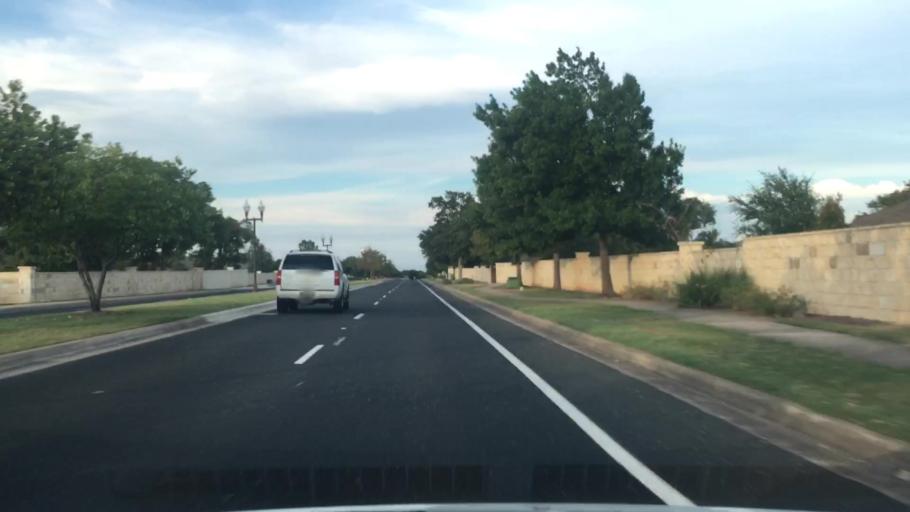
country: US
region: Texas
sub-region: Williamson County
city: Cedar Park
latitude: 30.4912
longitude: -97.7983
